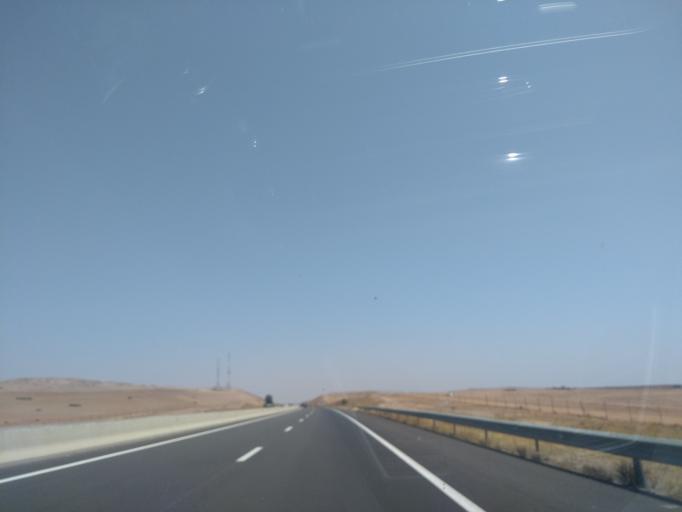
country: MA
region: Marrakech-Tensift-Al Haouz
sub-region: Kelaa-Des-Sraghna
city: Sidi Abdallah
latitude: 32.3032
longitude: -7.9591
